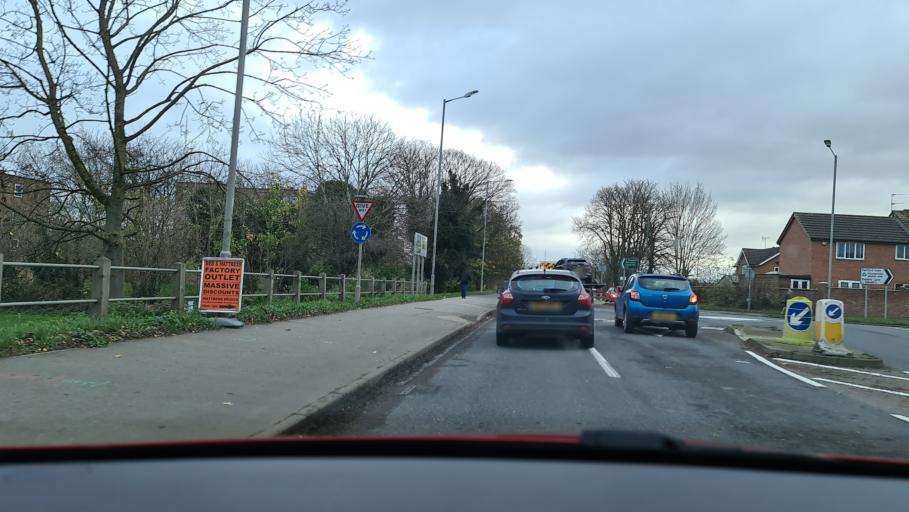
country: GB
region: England
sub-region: Buckinghamshire
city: Aylesbury
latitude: 51.8261
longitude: -0.8395
